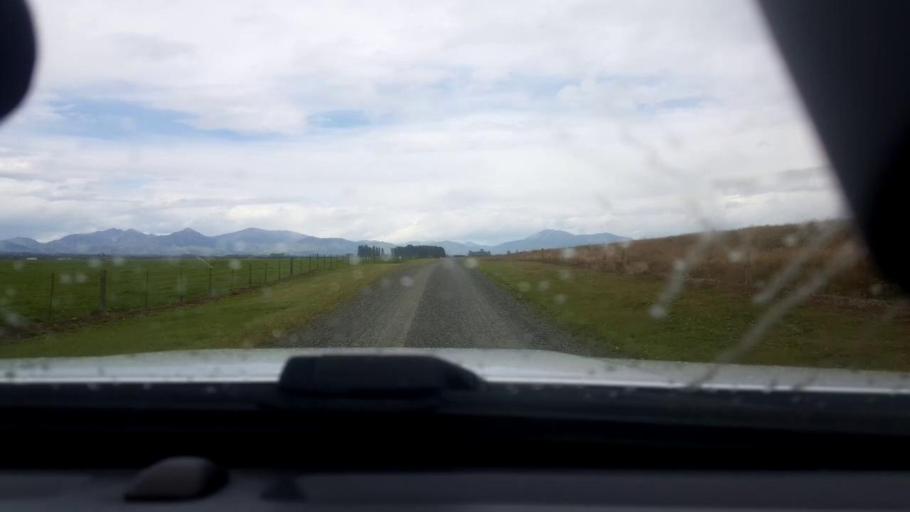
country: NZ
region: Canterbury
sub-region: Timaru District
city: Pleasant Point
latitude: -44.1188
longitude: 171.3595
